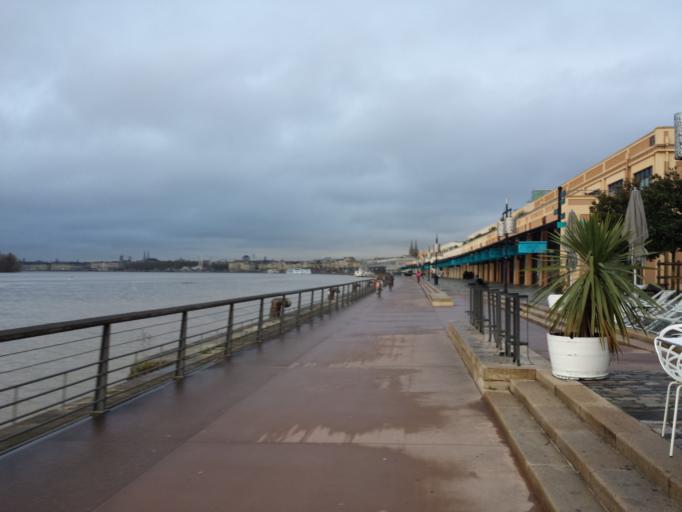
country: FR
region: Aquitaine
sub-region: Departement de la Gironde
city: Bordeaux
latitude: 44.8571
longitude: -0.5595
